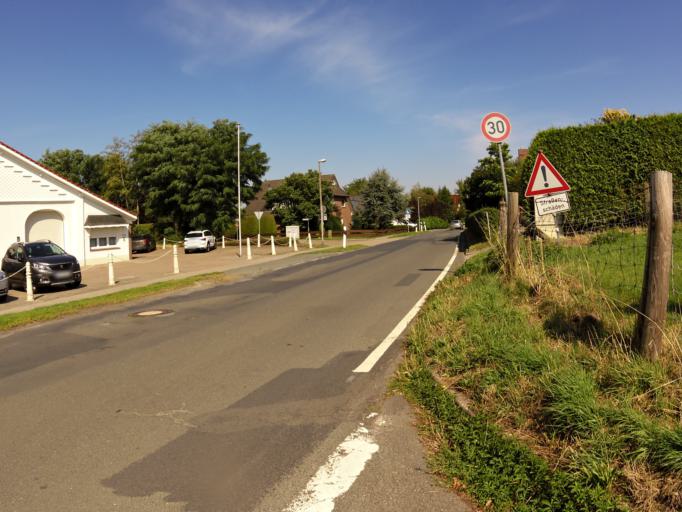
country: DE
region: Lower Saxony
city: Elsfleth
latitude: 53.2503
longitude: 8.4683
